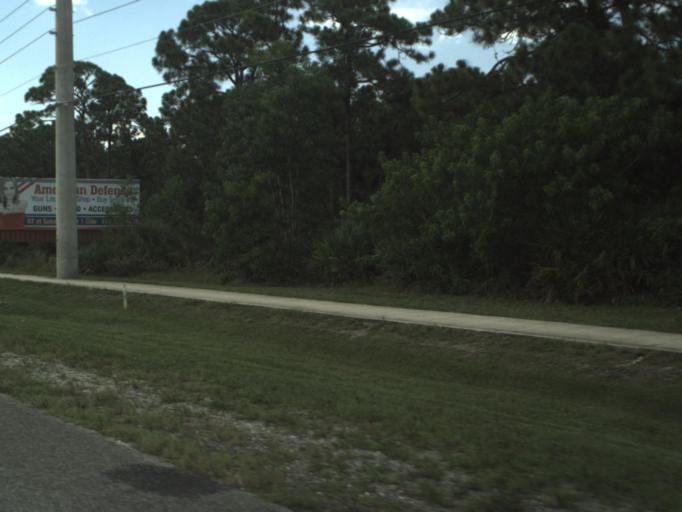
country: US
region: Florida
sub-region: Martin County
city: Port Salerno
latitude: 27.1260
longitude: -80.1940
